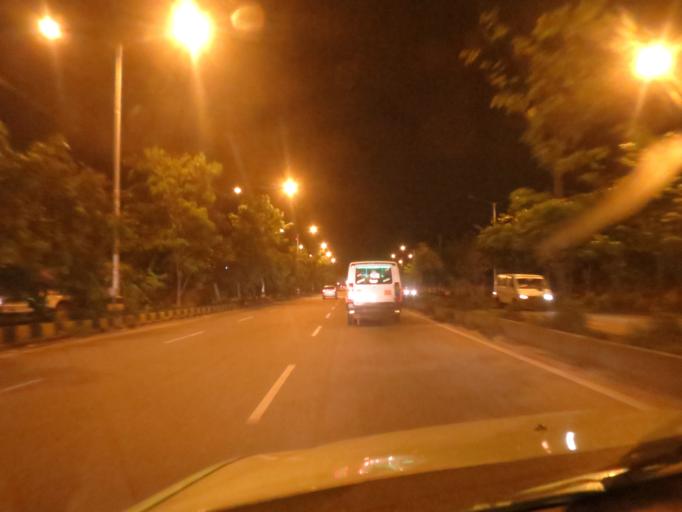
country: IN
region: Karnataka
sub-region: Bangalore Urban
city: Bangalore
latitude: 13.0057
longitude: 77.6630
